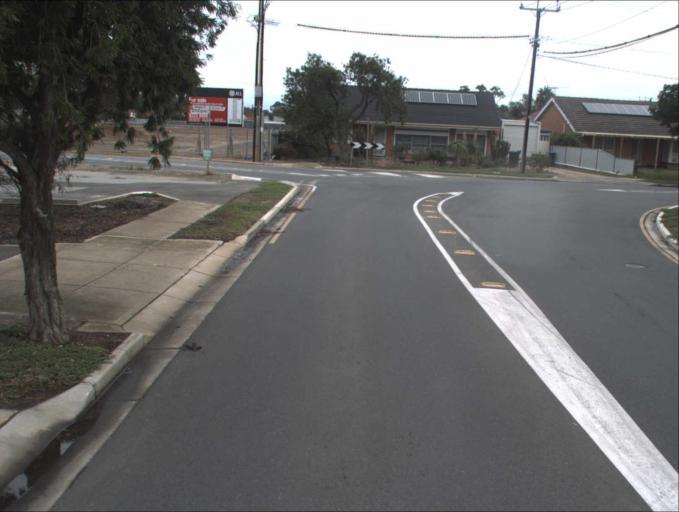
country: AU
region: South Australia
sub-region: Prospect
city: Prospect
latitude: -34.8784
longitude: 138.5804
